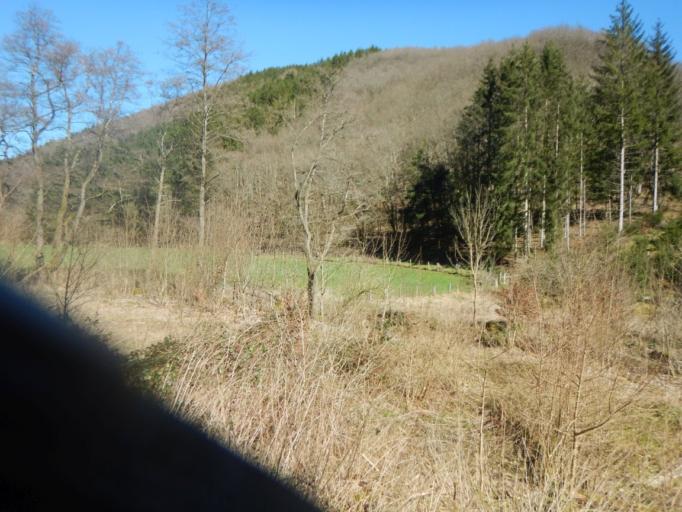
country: LU
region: Diekirch
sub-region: Canton de Wiltz
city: Eschweiler
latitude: 49.9776
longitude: 5.9687
